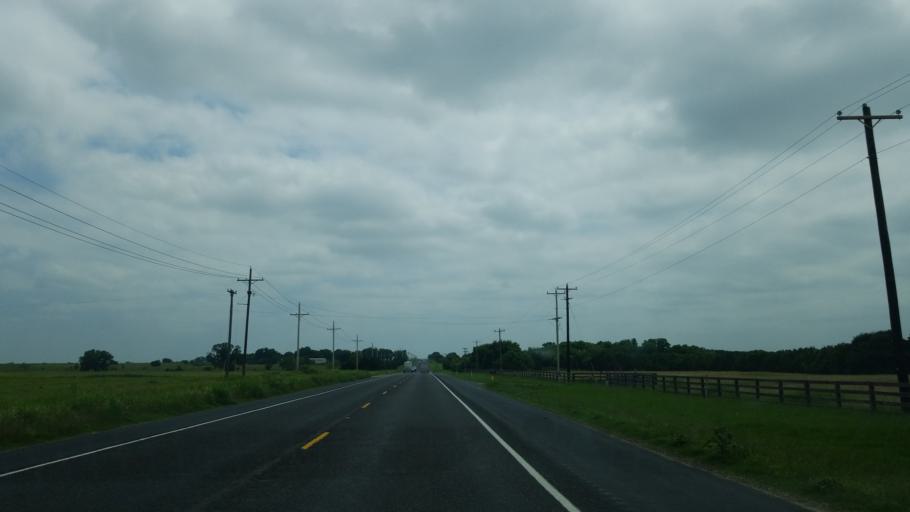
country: US
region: Texas
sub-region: Denton County
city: Pilot Point
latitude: 33.4365
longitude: -96.9288
